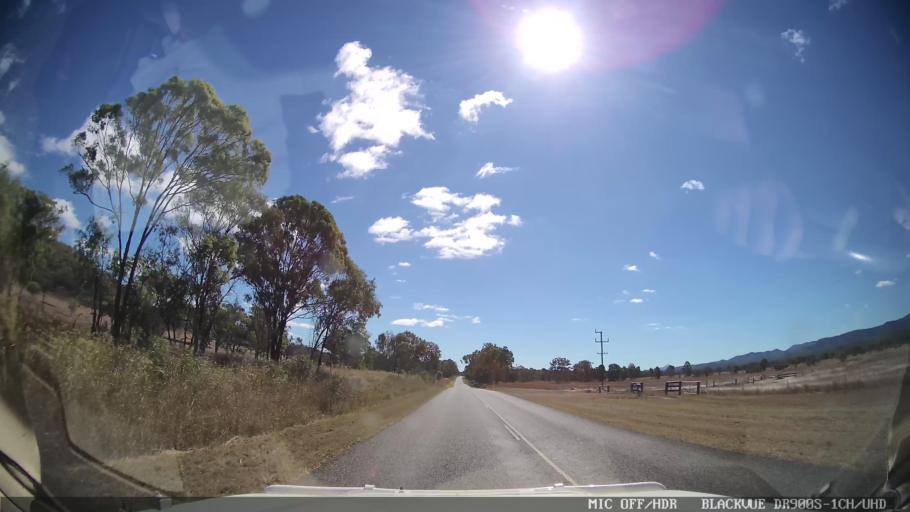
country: AU
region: Queensland
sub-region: Gladstone
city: Toolooa
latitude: -24.4496
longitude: 151.3448
